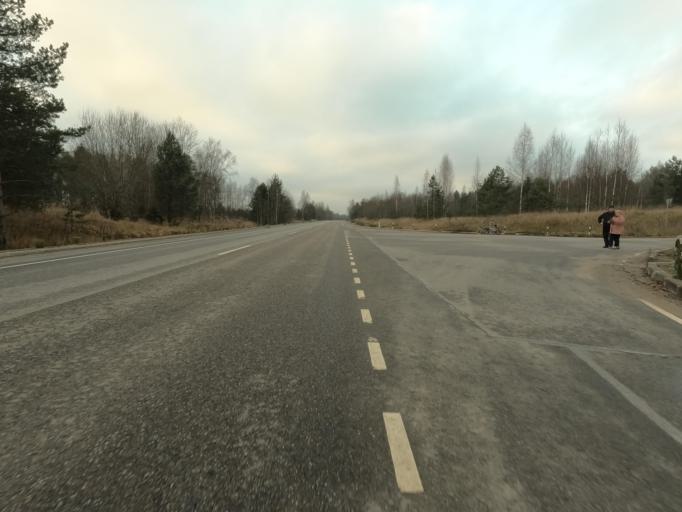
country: RU
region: Leningrad
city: Pavlovo
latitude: 59.8031
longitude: 30.9718
